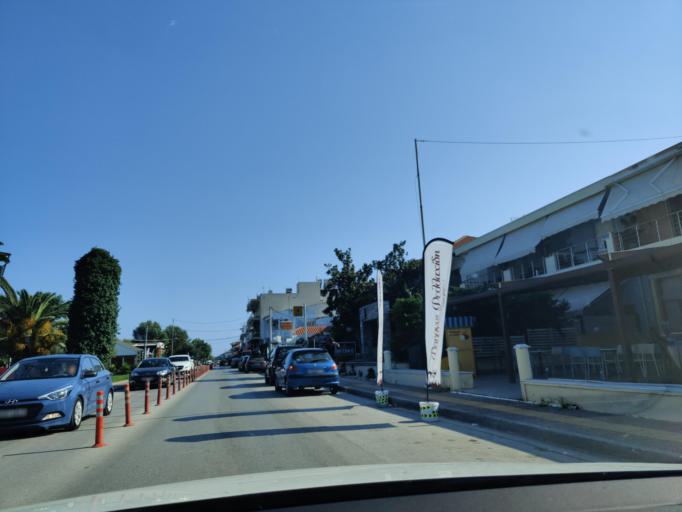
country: GR
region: East Macedonia and Thrace
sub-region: Nomos Kavalas
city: Nea Peramos
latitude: 40.8407
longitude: 24.3049
